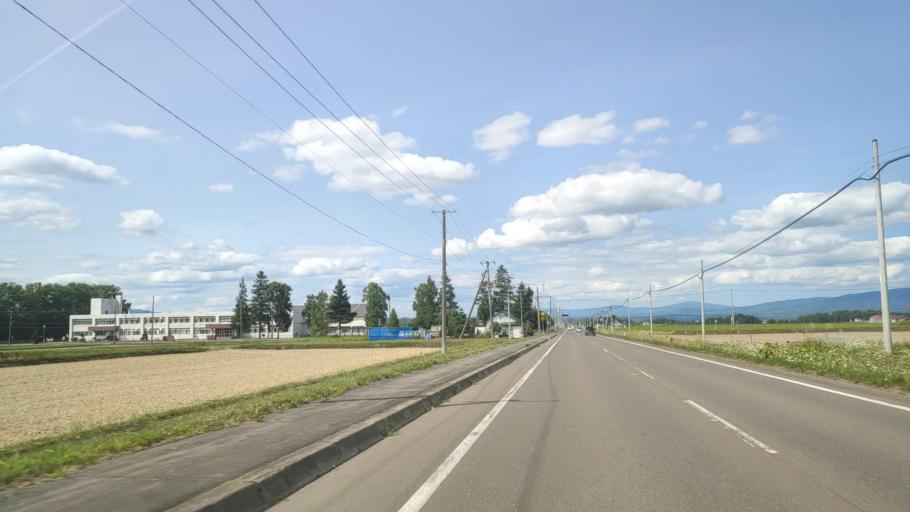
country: JP
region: Hokkaido
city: Nayoro
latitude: 44.2896
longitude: 142.4294
